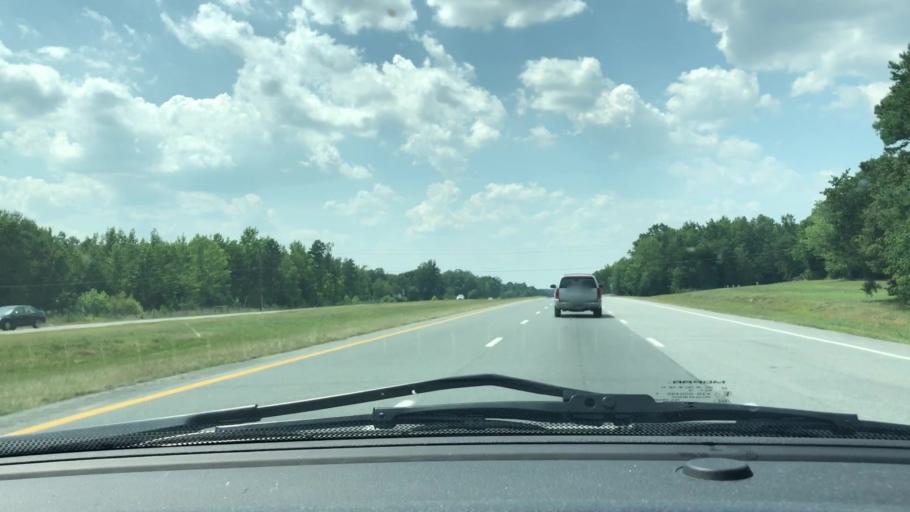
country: US
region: North Carolina
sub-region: Guilford County
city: Forest Oaks
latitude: 35.9661
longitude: -79.7088
